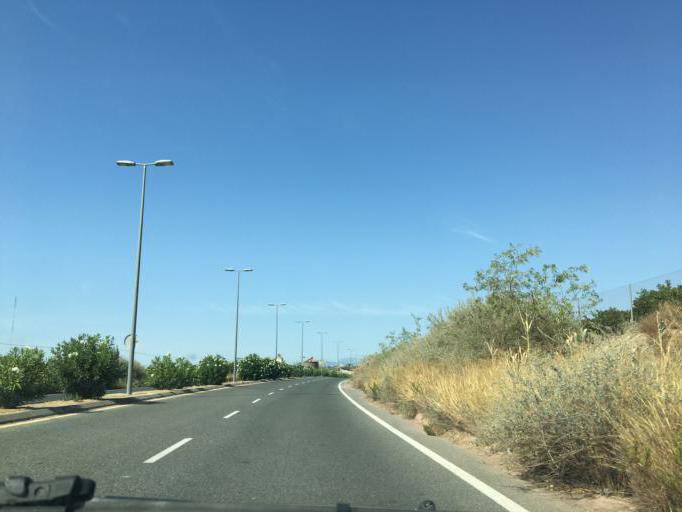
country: ES
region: Murcia
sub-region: Murcia
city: Murcia
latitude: 38.0461
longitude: -1.1300
